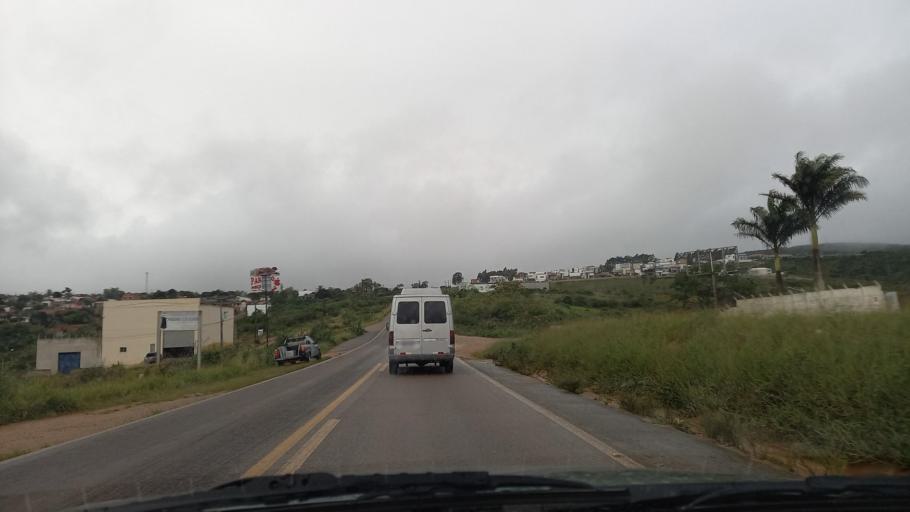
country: BR
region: Pernambuco
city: Garanhuns
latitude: -8.8616
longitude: -36.5108
